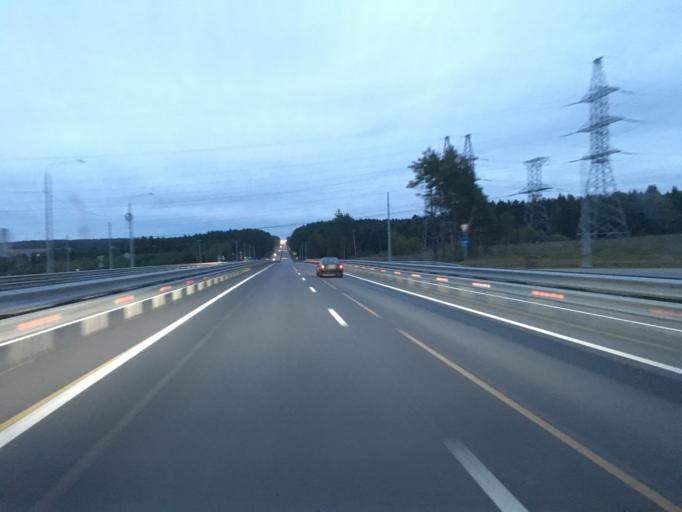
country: RU
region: Kaluga
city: Maloyaroslavets
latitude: 54.9575
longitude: 36.4578
